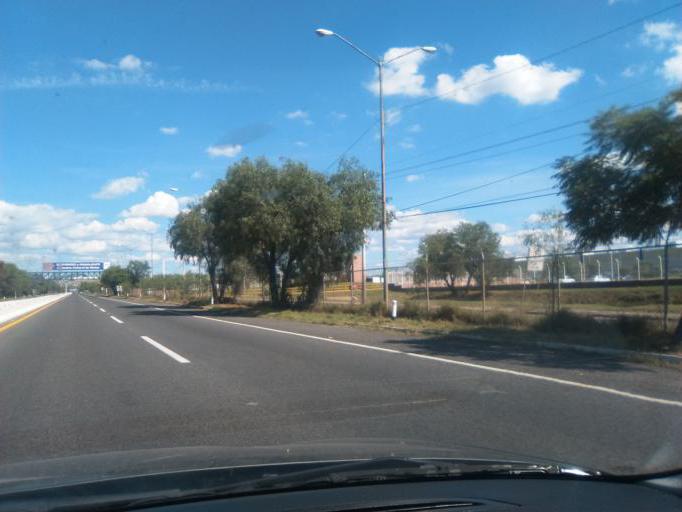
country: MX
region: Guanajuato
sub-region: Silao de la Victoria
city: Aguas Buenas
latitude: 20.9511
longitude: -101.3890
